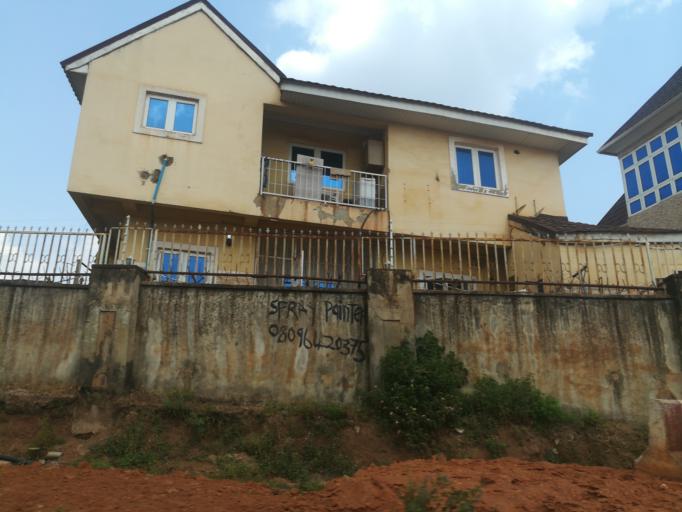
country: NG
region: Abuja Federal Capital Territory
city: Abuja
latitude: 9.0578
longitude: 7.4472
